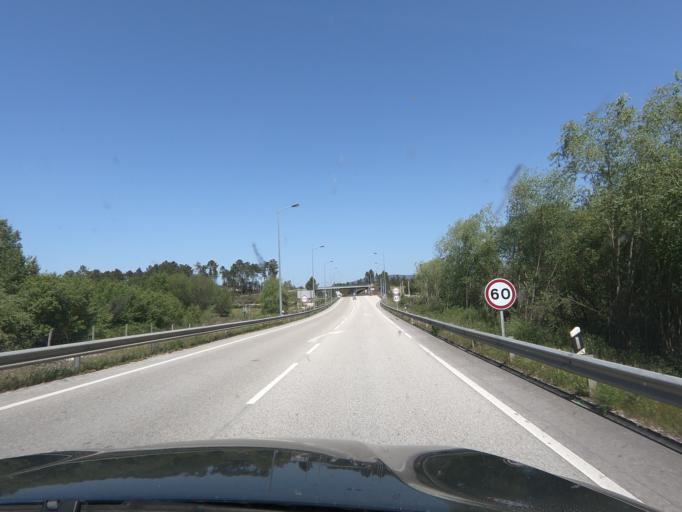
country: PT
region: Coimbra
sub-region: Lousa
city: Lousa
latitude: 40.1251
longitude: -8.2771
